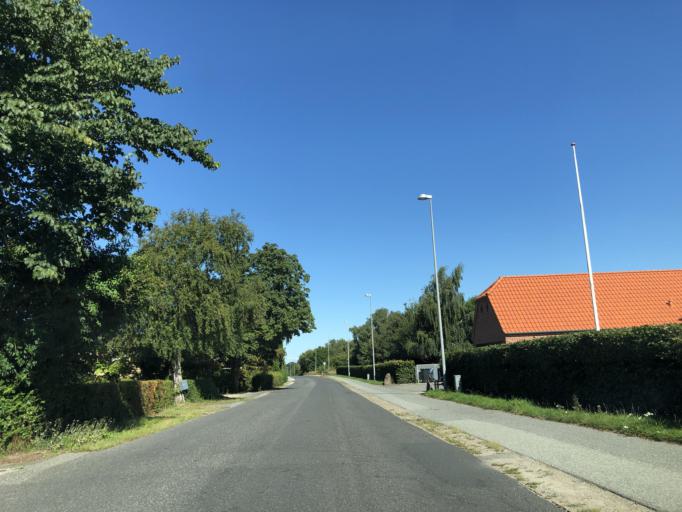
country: DK
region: North Denmark
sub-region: Mariagerfjord Kommune
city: Hobro
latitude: 56.6448
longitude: 9.7795
